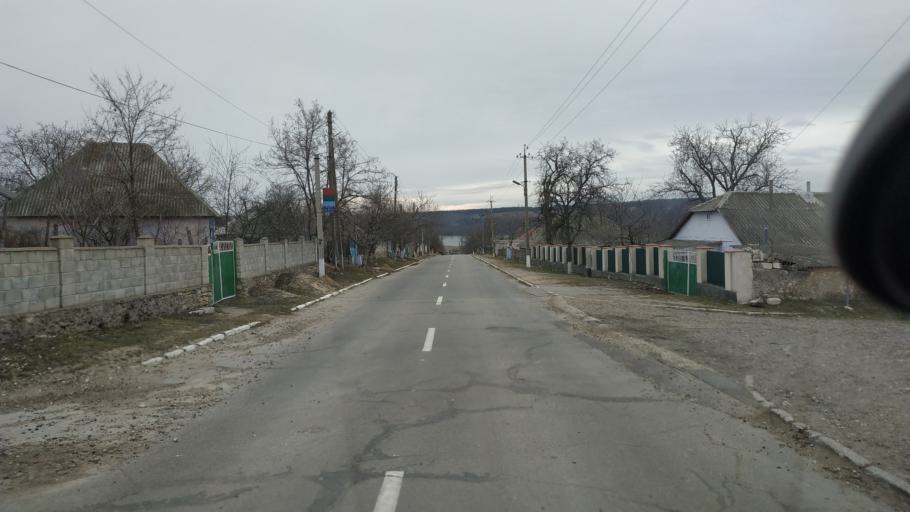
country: MD
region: Telenesti
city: Cocieri
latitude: 47.3474
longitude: 29.1176
